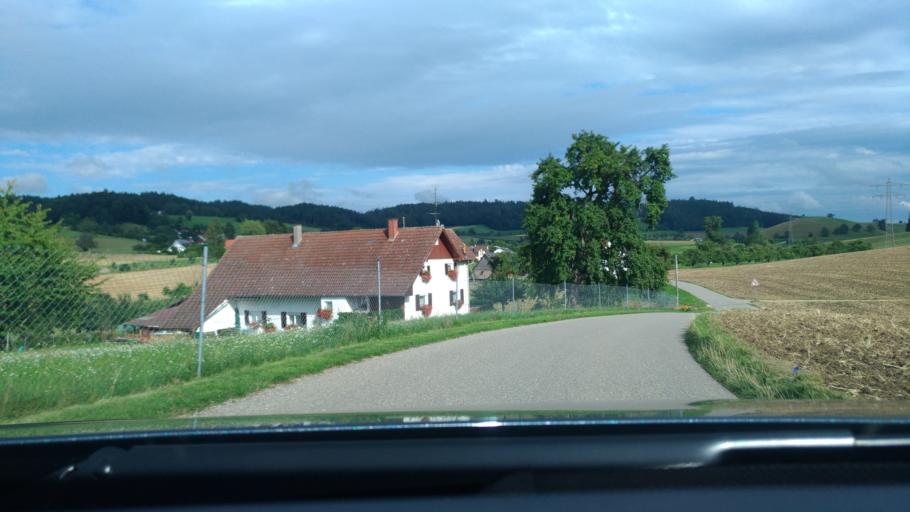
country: DE
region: Baden-Wuerttemberg
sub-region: Tuebingen Region
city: Sipplingen
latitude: 47.8170
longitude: 9.1071
